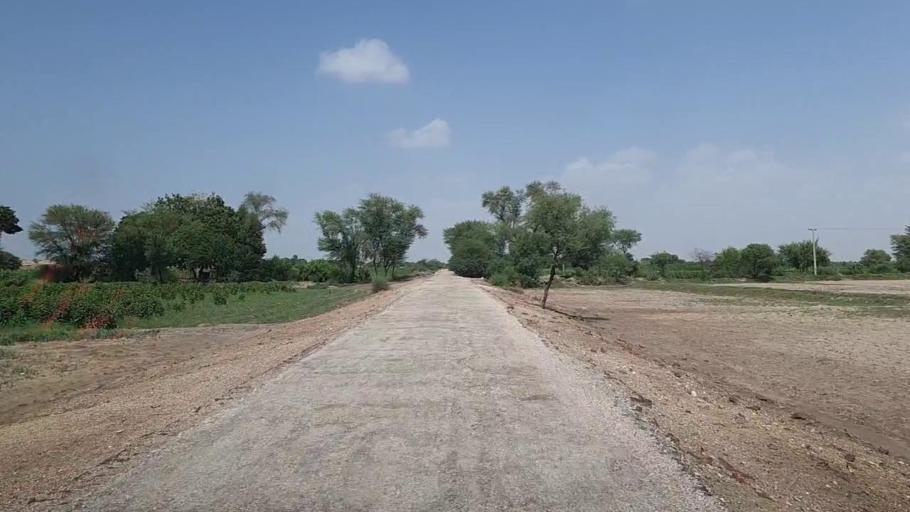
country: PK
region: Sindh
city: Pad Idan
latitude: 26.8027
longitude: 68.3731
